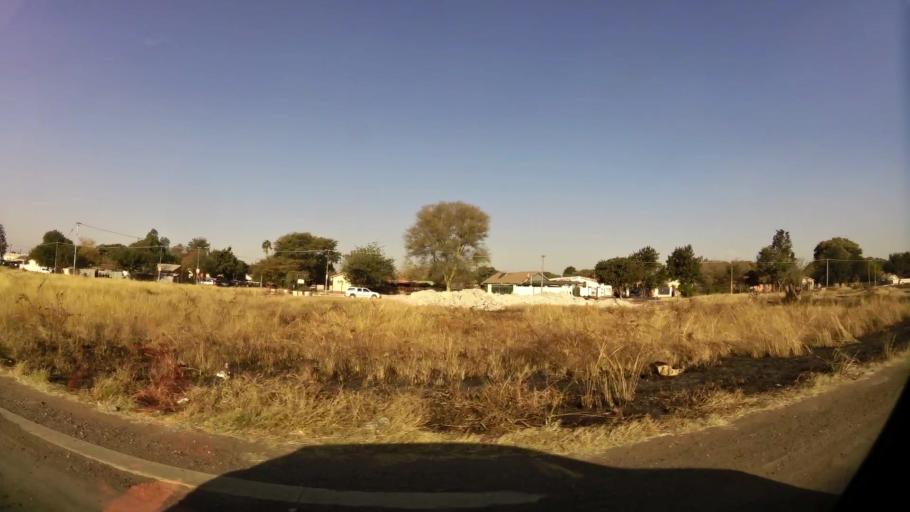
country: ZA
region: North-West
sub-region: Bojanala Platinum District Municipality
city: Rustenburg
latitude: -25.6451
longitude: 27.2287
